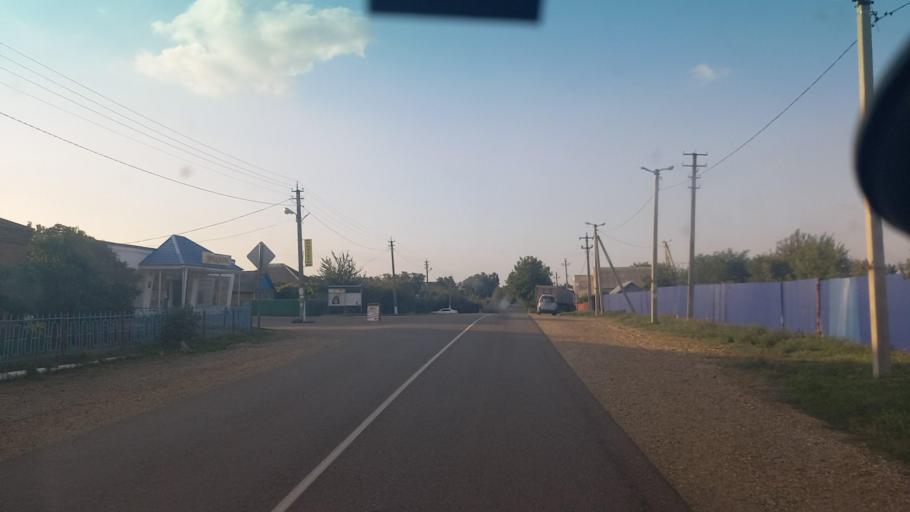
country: RU
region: Adygeya
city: Khatukay
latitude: 45.2944
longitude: 39.5573
